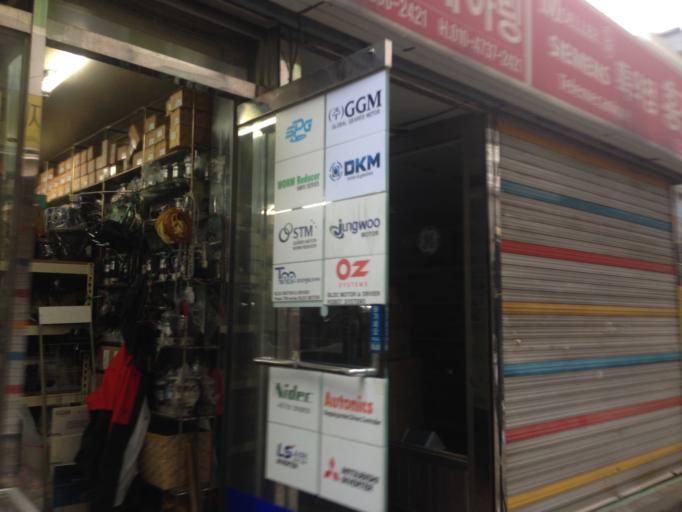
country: KR
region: Seoul
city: Seoul
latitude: 37.5693
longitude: 126.9930
